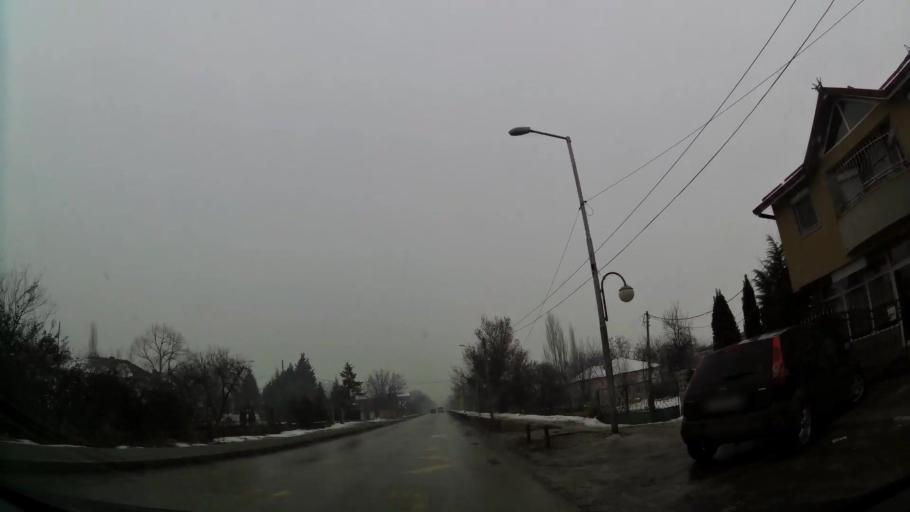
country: MK
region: Petrovec
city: Petrovec
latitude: 41.9288
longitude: 21.6271
